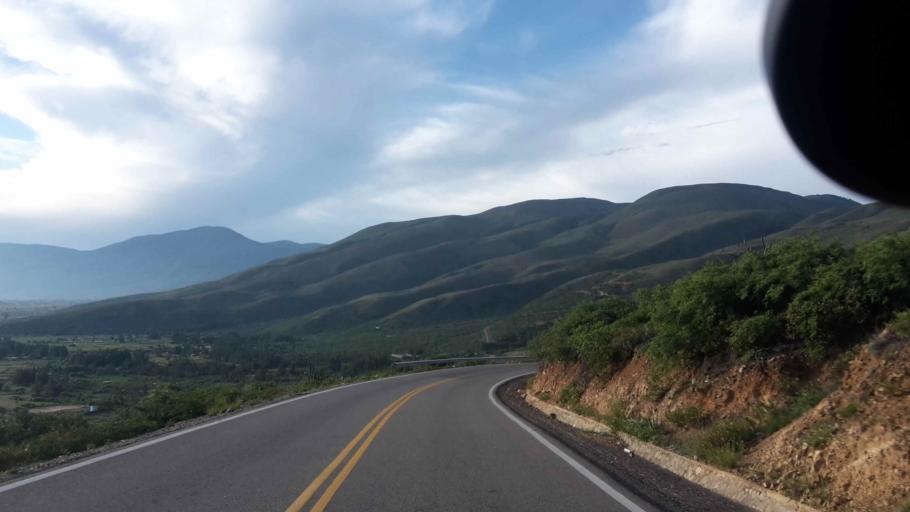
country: BO
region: Cochabamba
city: Arani
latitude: -17.5798
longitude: -65.7526
